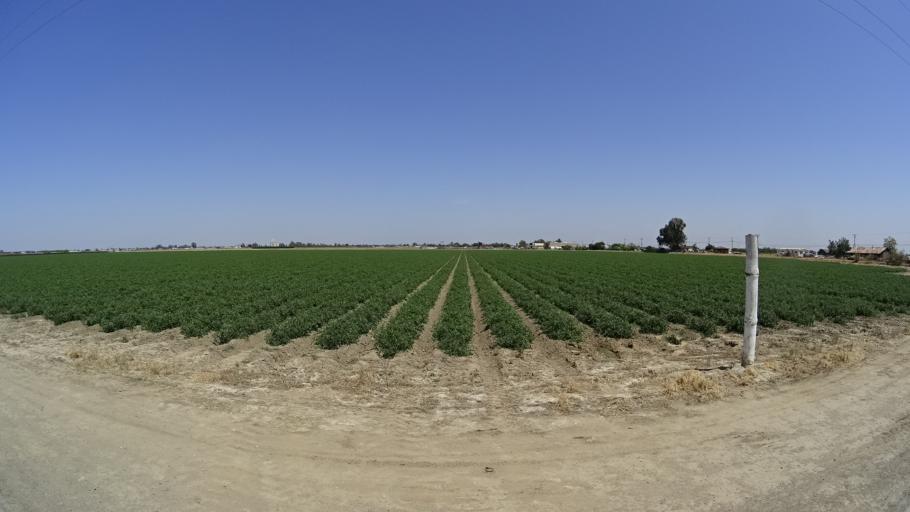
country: US
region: California
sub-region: Kings County
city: Home Garden
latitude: 36.2841
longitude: -119.6389
